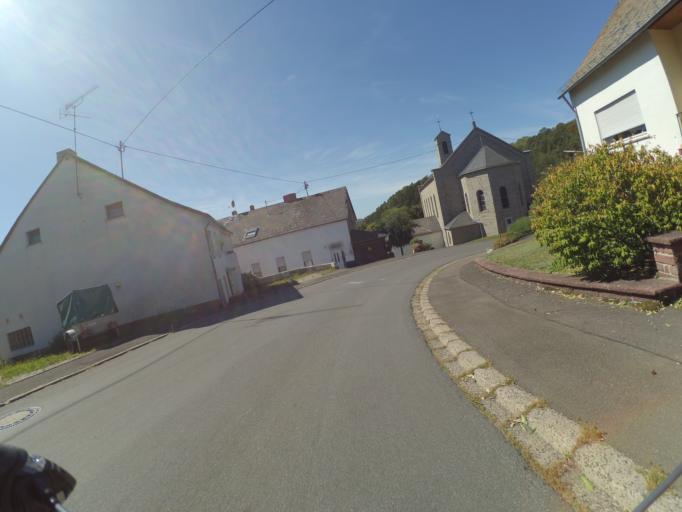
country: DE
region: Rheinland-Pfalz
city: Rorodt
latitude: 49.7733
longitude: 7.0884
